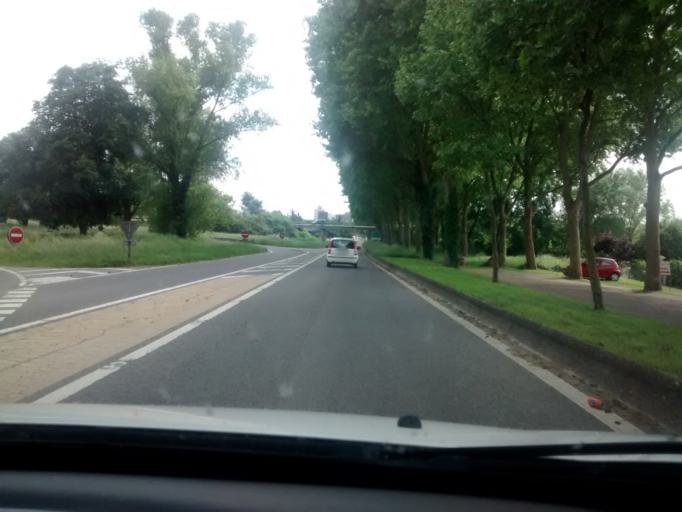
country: FR
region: Ile-de-France
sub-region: Departement des Yvelines
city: Saint-Cyr-l'Ecole
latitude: 48.7962
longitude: 2.0548
